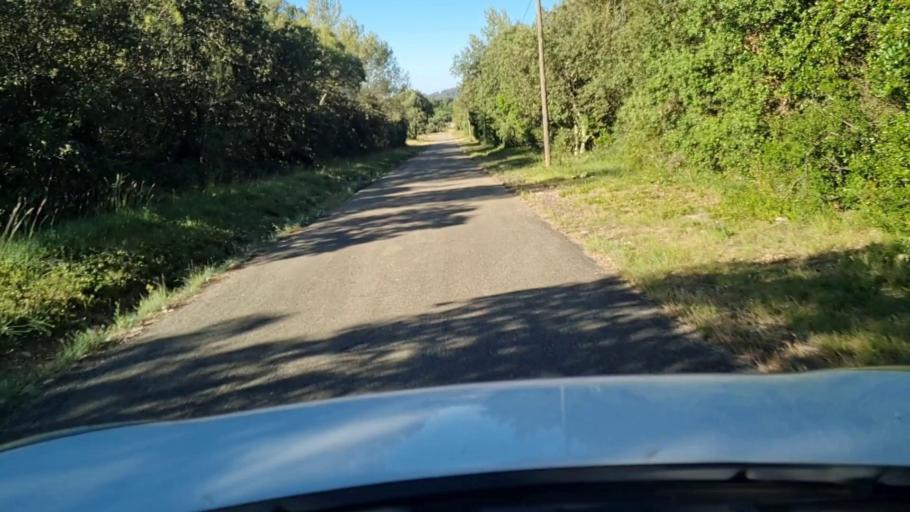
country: FR
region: Languedoc-Roussillon
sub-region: Departement du Gard
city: Villevieille
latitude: 43.8454
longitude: 4.0785
